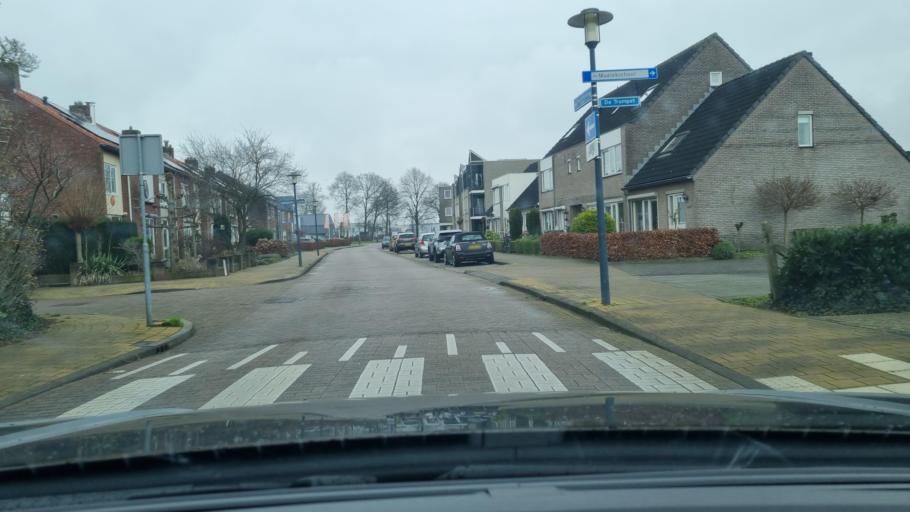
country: NL
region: Gelderland
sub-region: Gemeente Montferland
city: s-Heerenberg
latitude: 51.8746
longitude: 6.2518
